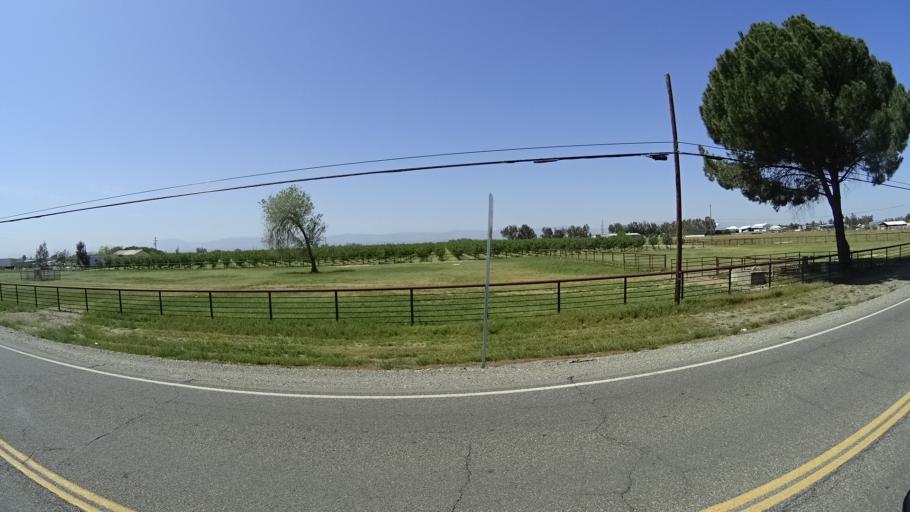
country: US
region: California
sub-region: Glenn County
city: Orland
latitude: 39.6927
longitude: -122.1966
